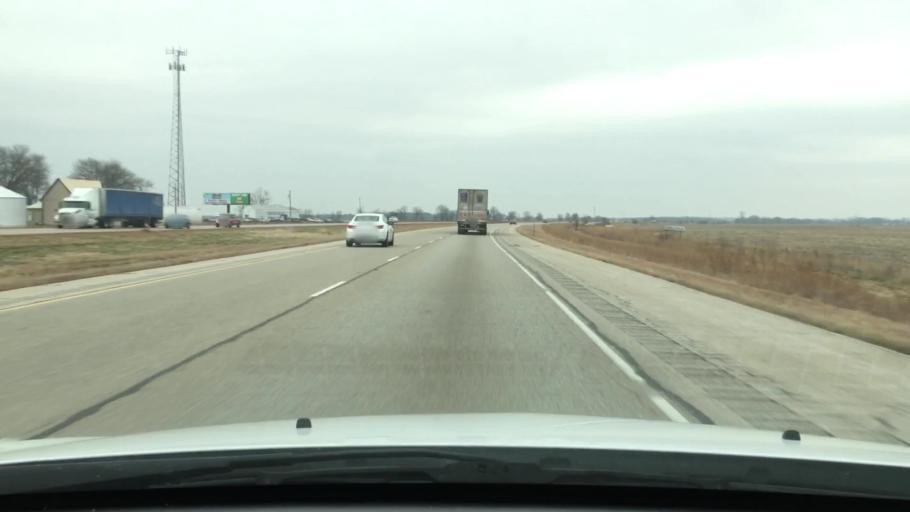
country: US
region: Illinois
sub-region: Logan County
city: Atlanta
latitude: 40.3228
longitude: -89.1562
